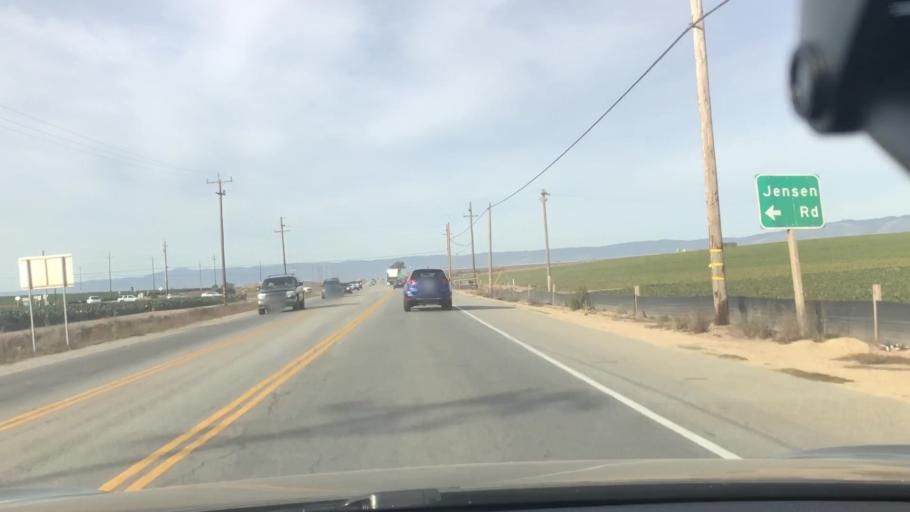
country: US
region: California
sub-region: Monterey County
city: Las Lomas
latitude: 36.8523
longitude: -121.7711
